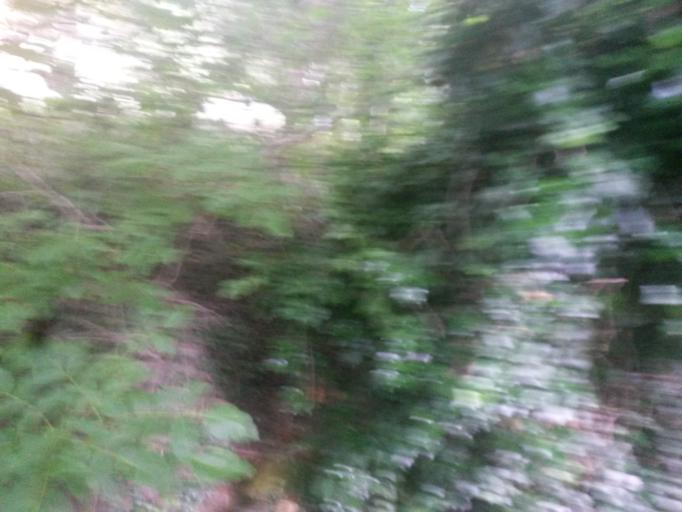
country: GR
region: North Aegean
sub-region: Nomos Lesvou
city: Agiasos
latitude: 39.0972
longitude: 26.3985
